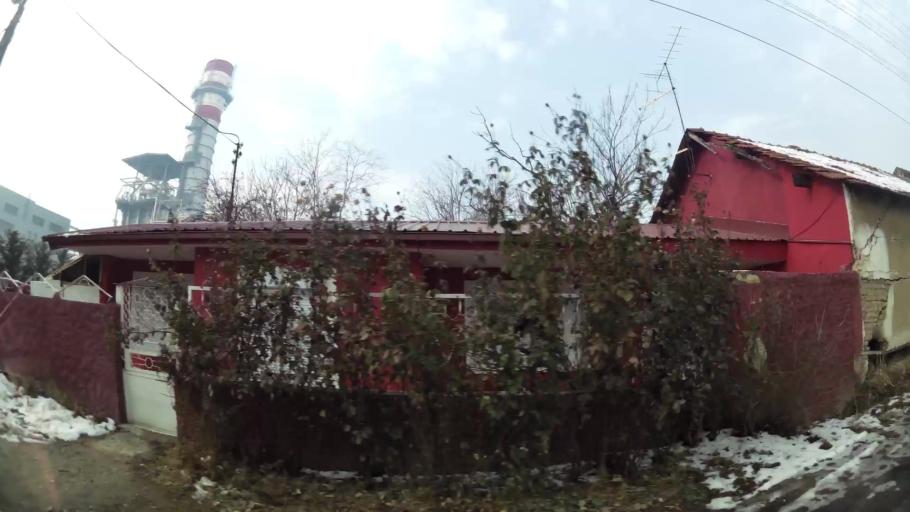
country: MK
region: Karpos
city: Skopje
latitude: 41.9949
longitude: 21.4538
